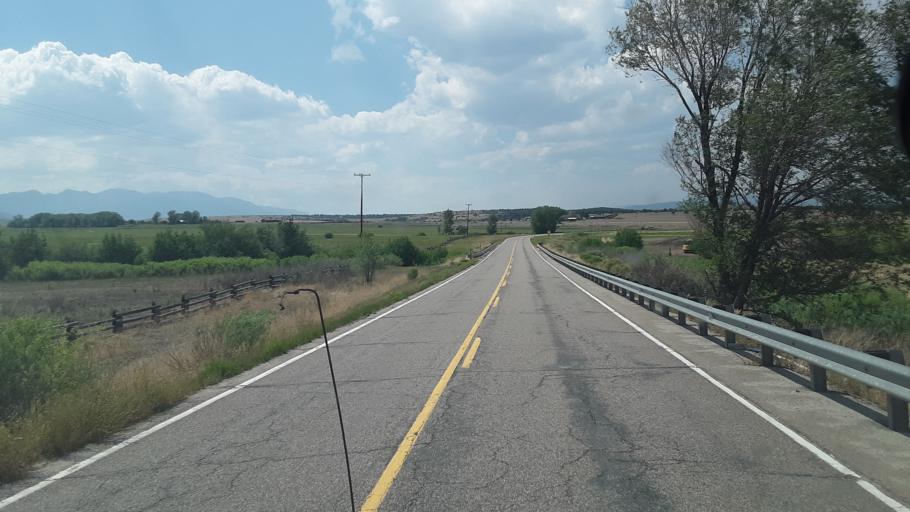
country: US
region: Colorado
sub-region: Custer County
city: Westcliffe
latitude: 38.2876
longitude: -105.6178
